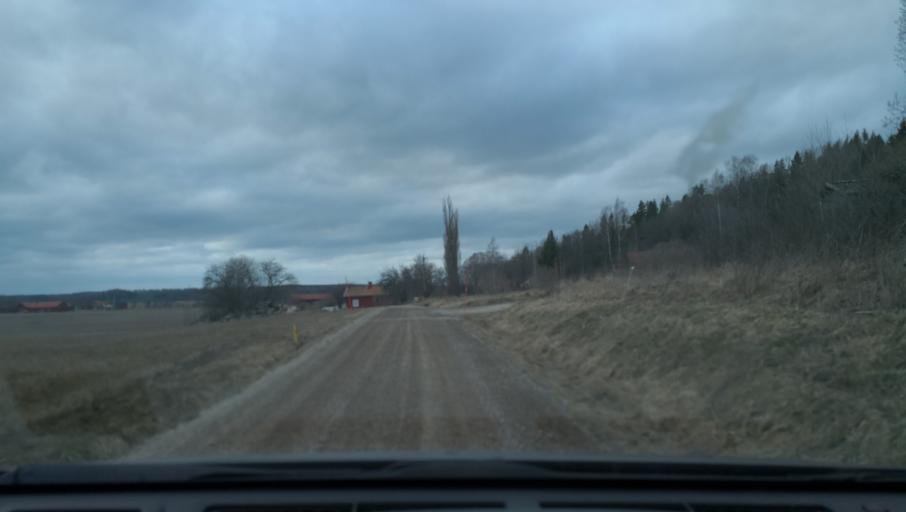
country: SE
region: Vaestmanland
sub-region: Kopings Kommun
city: Koping
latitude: 59.5320
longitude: 15.9041
